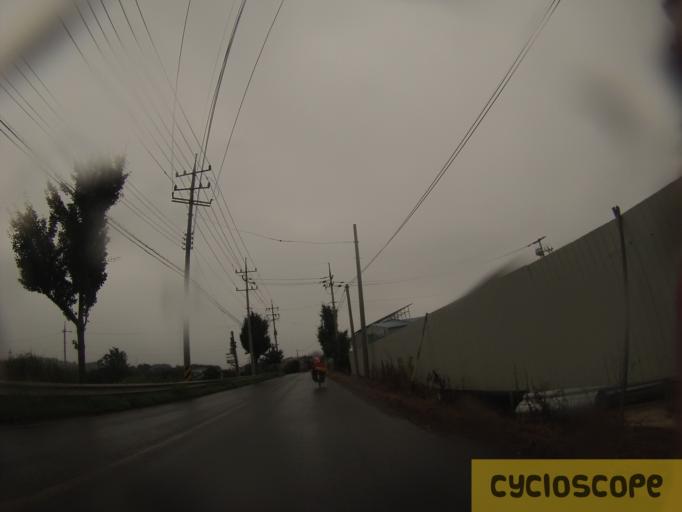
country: KR
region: Chungcheongnam-do
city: Taisen-ri
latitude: 36.1991
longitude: 126.5365
